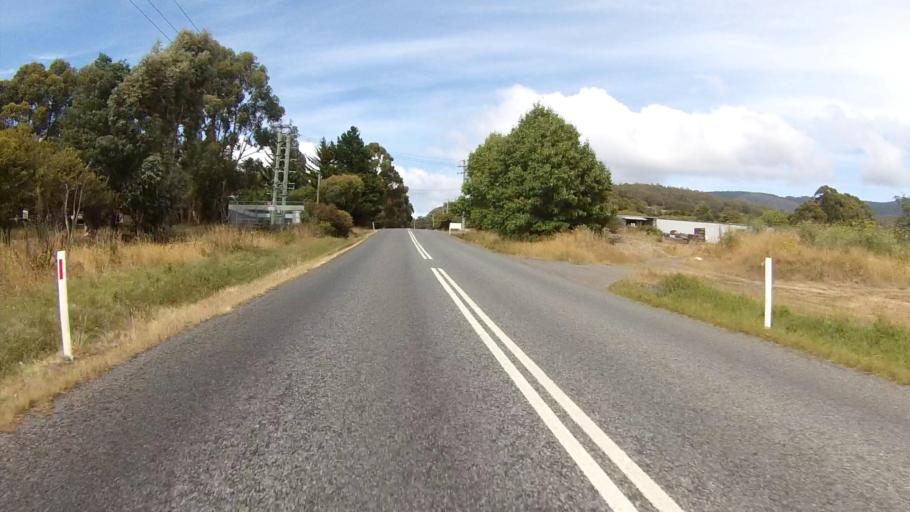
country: AU
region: Tasmania
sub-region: Kingborough
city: Kettering
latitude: -43.1376
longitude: 147.2459
